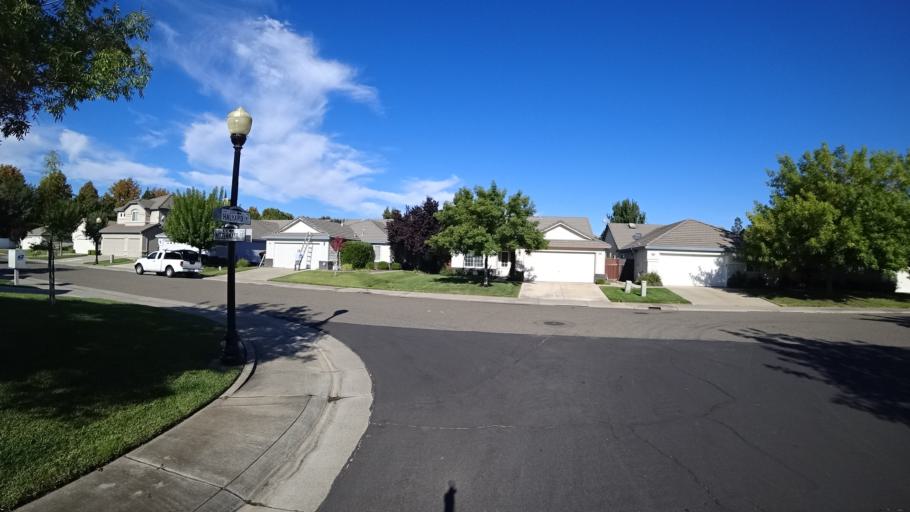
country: US
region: California
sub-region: Sacramento County
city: Laguna
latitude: 38.4061
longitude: -121.4716
